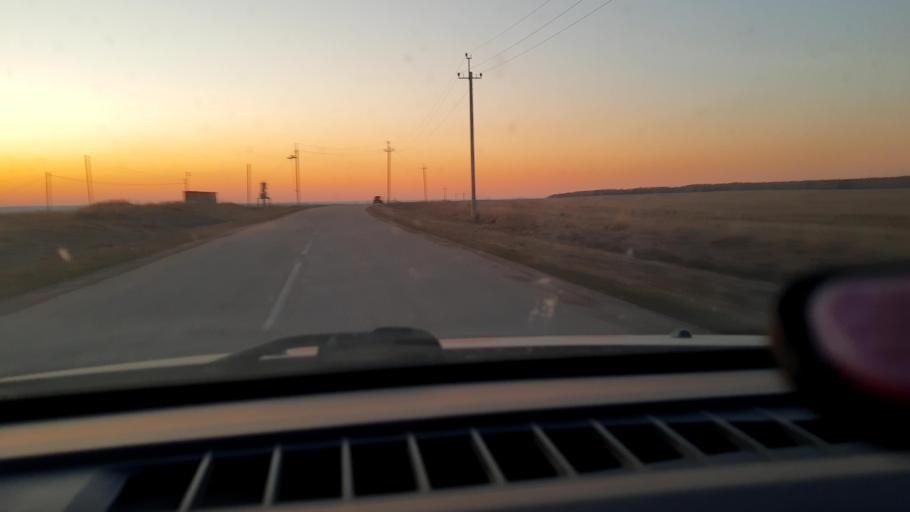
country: RU
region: Bashkortostan
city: Asanovo
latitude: 54.8067
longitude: 55.4865
